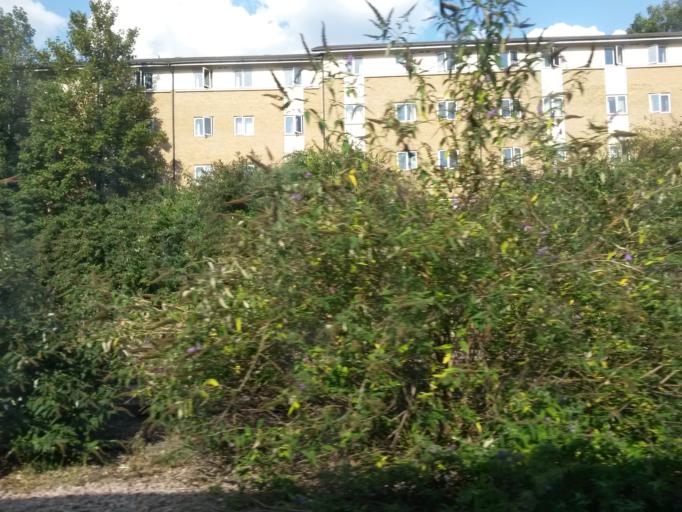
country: GB
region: England
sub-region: Greater London
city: Catford
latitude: 51.4740
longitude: -0.0398
